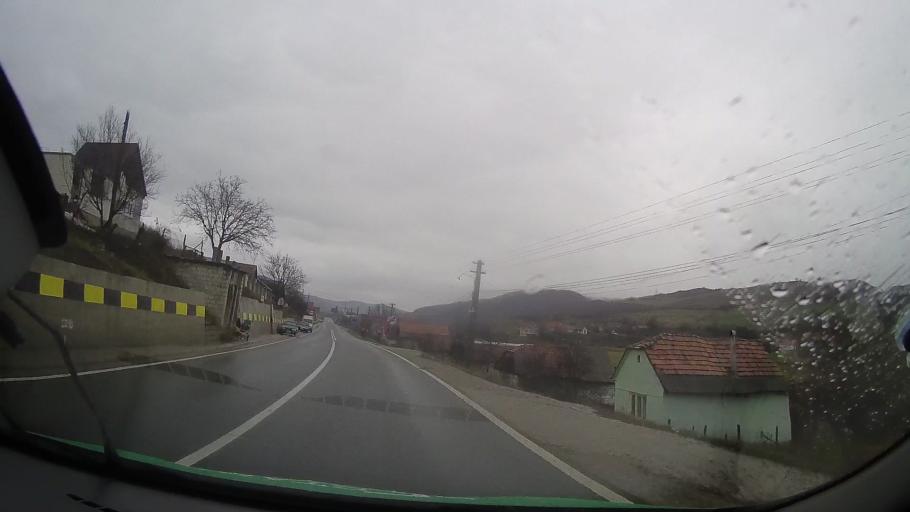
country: RO
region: Bistrita-Nasaud
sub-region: Comuna Galatii Bistritei
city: Galatii Bistritei
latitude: 46.9503
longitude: 24.4507
